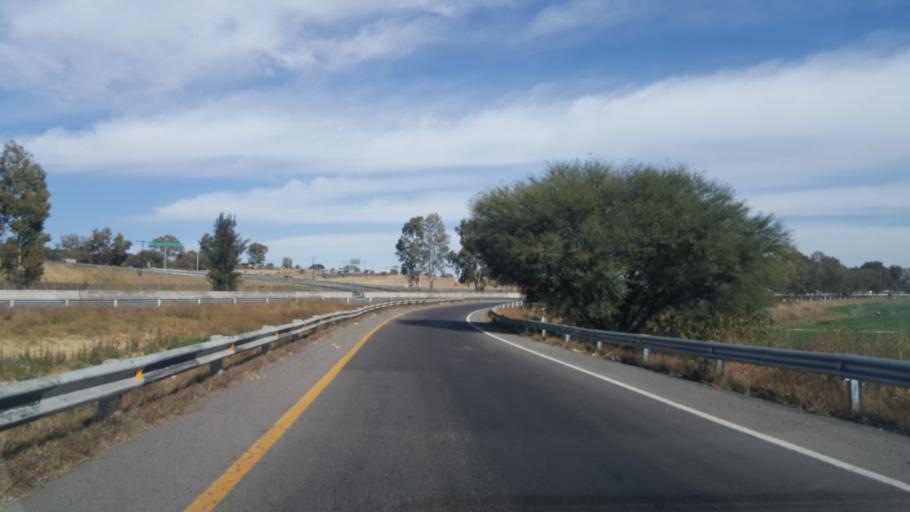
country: MX
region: Jalisco
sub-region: Lagos de Moreno
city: Cristeros [Fraccionamiento]
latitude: 21.3166
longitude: -102.0450
